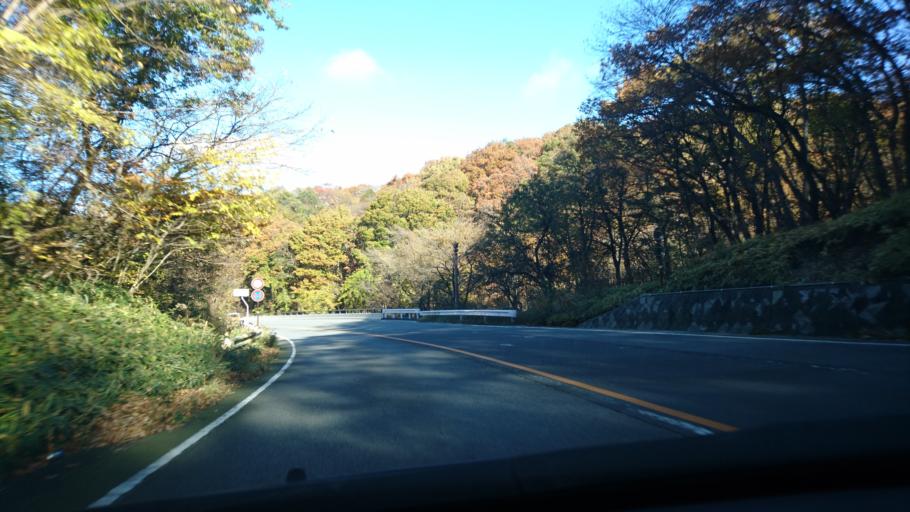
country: JP
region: Nagano
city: Saku
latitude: 36.3254
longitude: 138.6484
